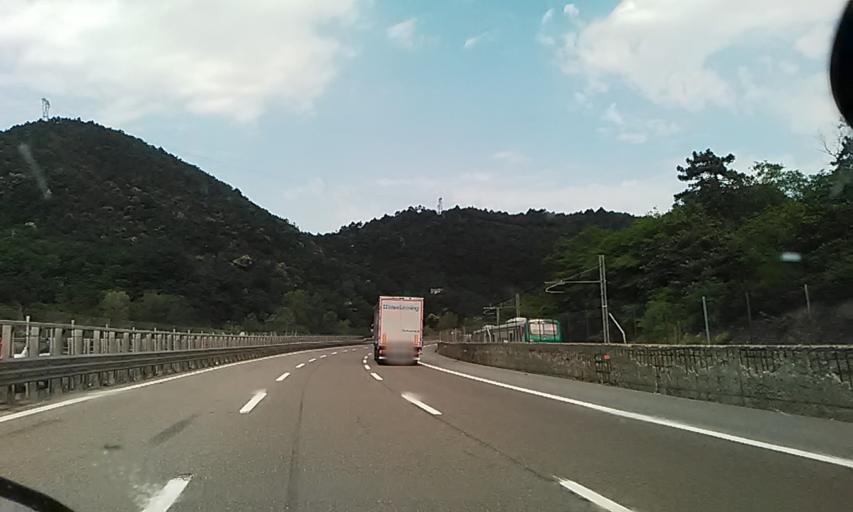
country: IT
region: Piedmont
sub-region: Provincia di Alessandria
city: Belforte Monferrato
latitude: 44.6030
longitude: 8.6644
